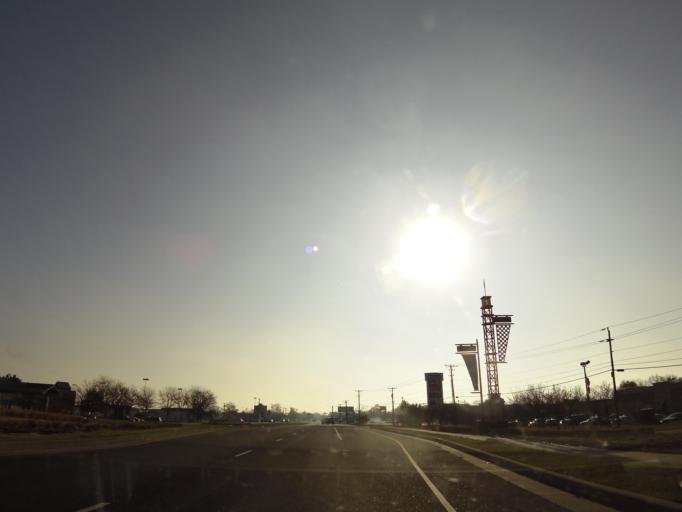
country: US
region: Indiana
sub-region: Marion County
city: Speedway
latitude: 39.8009
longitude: -86.2685
